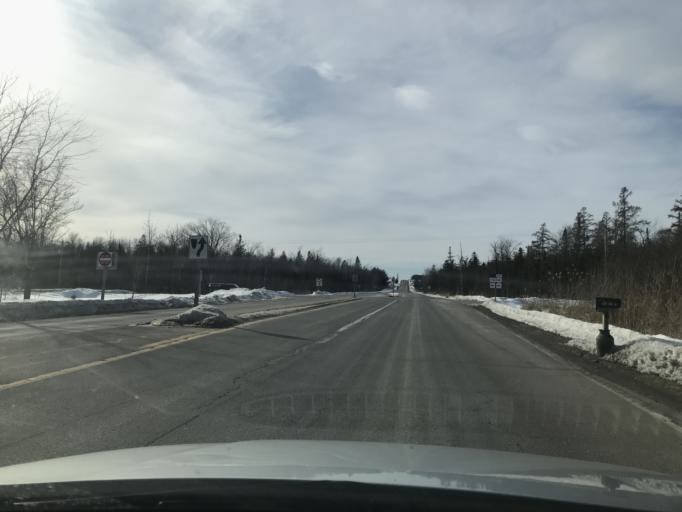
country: US
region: Wisconsin
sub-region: Oconto County
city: Oconto Falls
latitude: 45.1089
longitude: -88.0325
